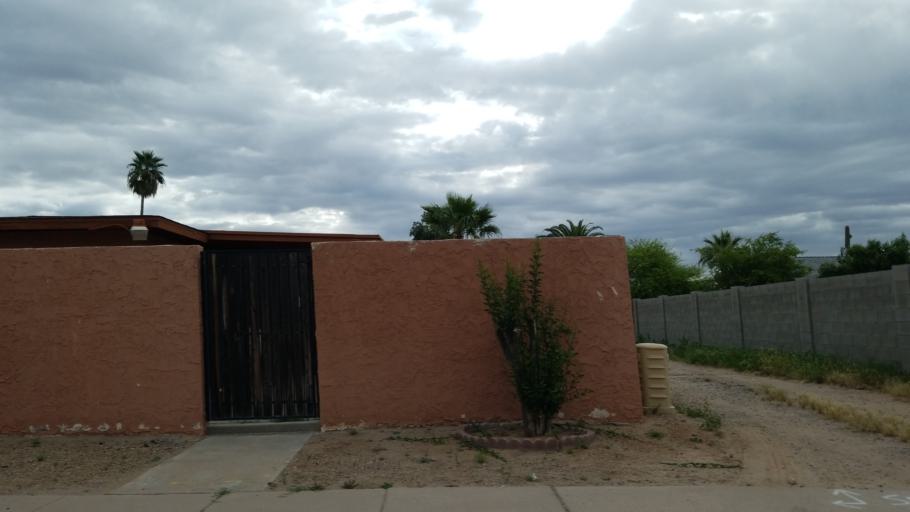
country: US
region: Arizona
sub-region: Maricopa County
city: Paradise Valley
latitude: 33.5987
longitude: -112.0305
